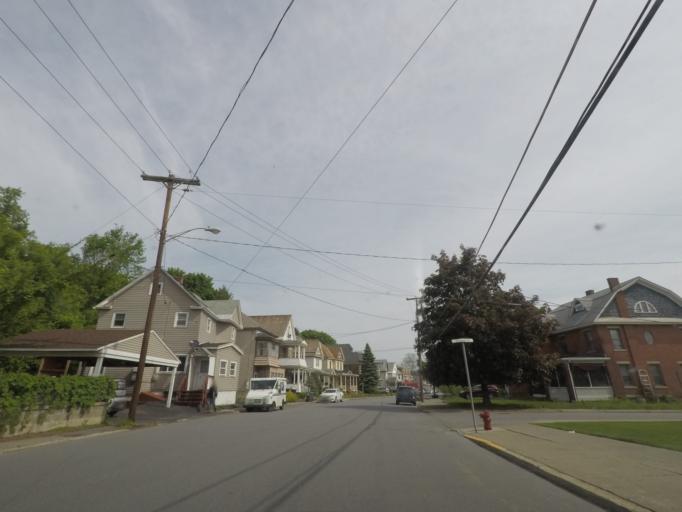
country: US
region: New York
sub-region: Saratoga County
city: Mechanicville
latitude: 42.9005
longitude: -73.6882
